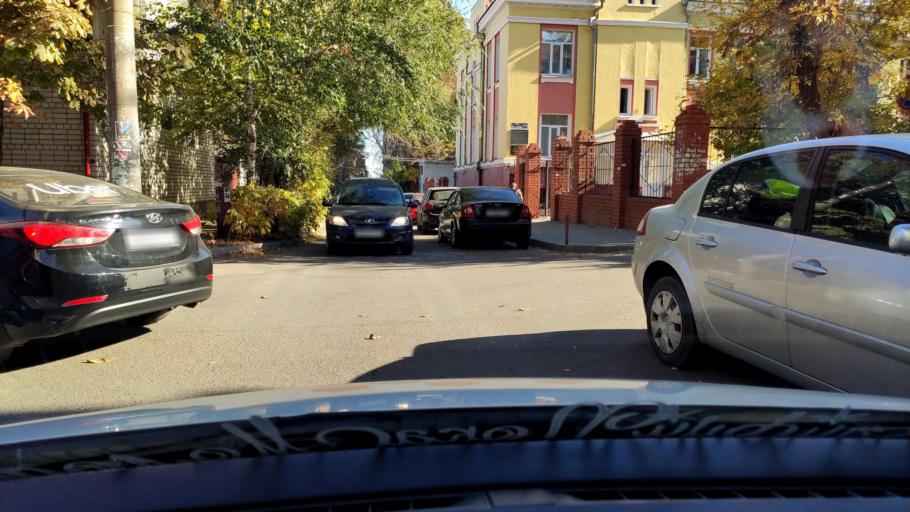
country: RU
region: Voronezj
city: Voronezh
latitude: 51.6730
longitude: 39.2205
